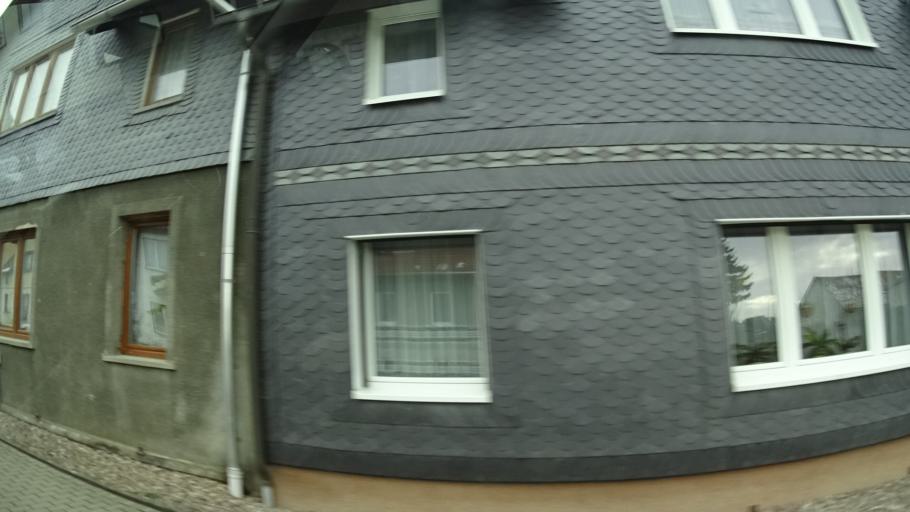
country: DE
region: Thuringia
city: Pennewitz
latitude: 50.6993
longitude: 11.0150
